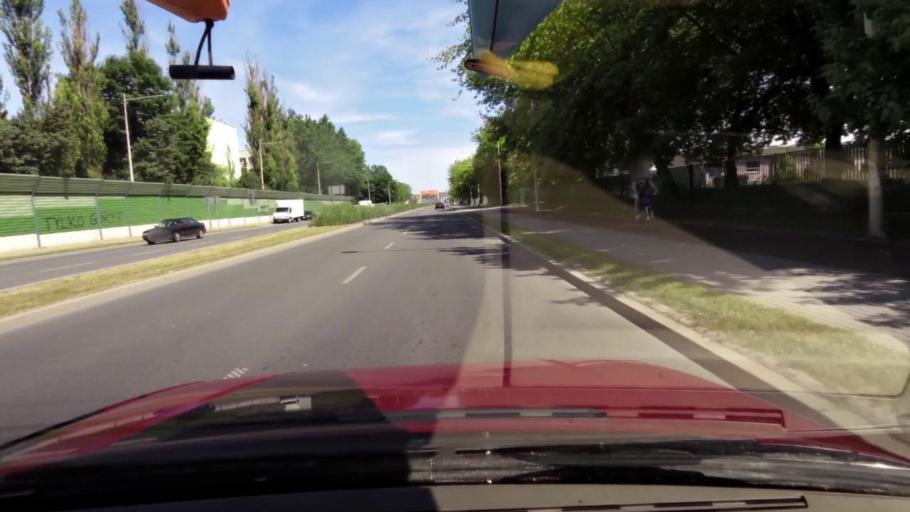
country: PL
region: Pomeranian Voivodeship
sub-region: Powiat slupski
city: Kobylnica
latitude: 54.4563
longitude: 17.0025
